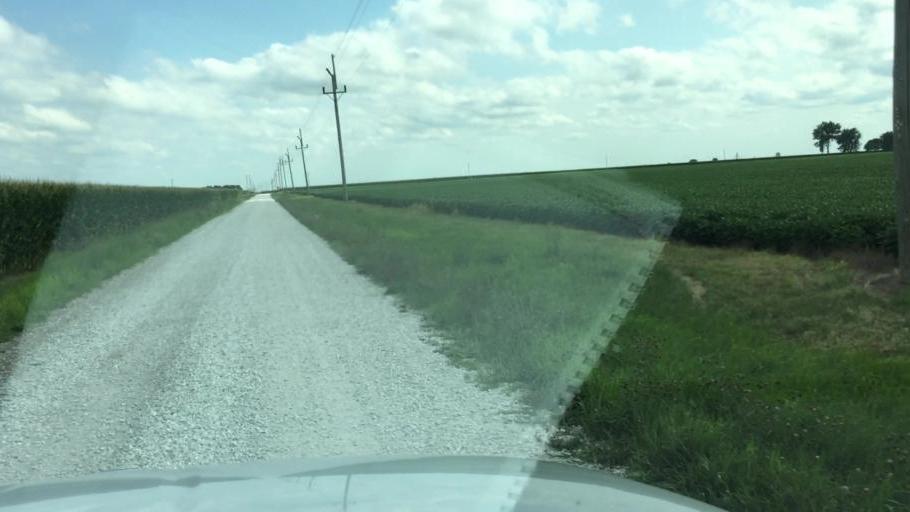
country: US
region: Illinois
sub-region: Hancock County
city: Carthage
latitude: 40.4099
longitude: -91.1786
